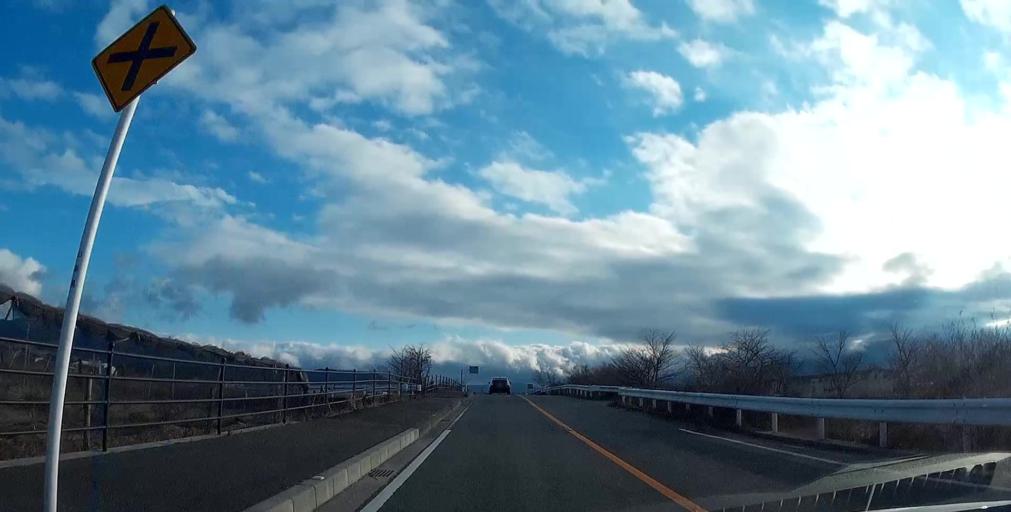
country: JP
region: Yamanashi
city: Fujikawaguchiko
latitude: 35.4648
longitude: 138.8419
